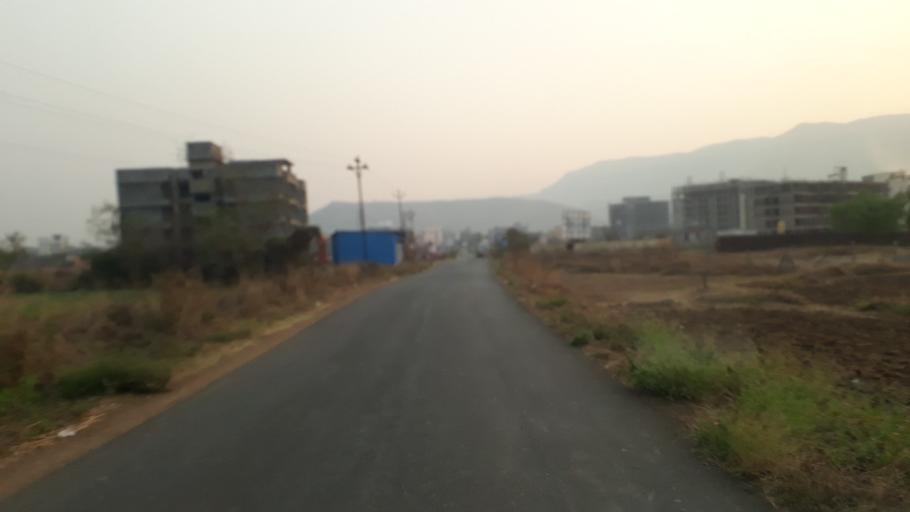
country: IN
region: Maharashtra
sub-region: Raigarh
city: Neral
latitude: 19.0359
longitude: 73.3275
